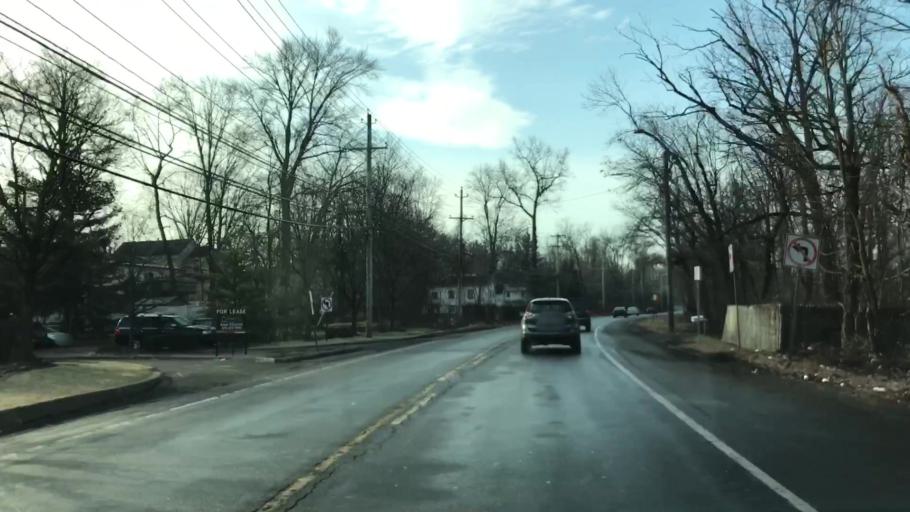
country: US
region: New York
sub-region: Rockland County
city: Congers
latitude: 41.1459
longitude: -73.9345
